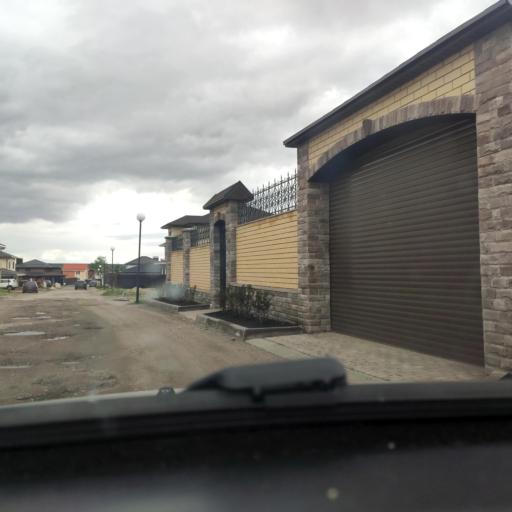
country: RU
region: Voronezj
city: Podgornoye
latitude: 51.7554
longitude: 39.1458
